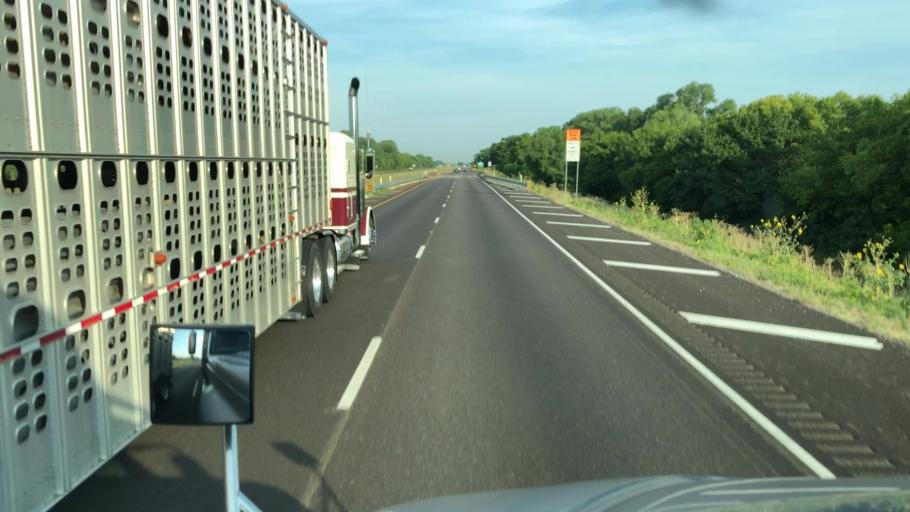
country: US
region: Texas
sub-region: McLennan County
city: Bellmead
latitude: 31.5398
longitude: -97.0443
